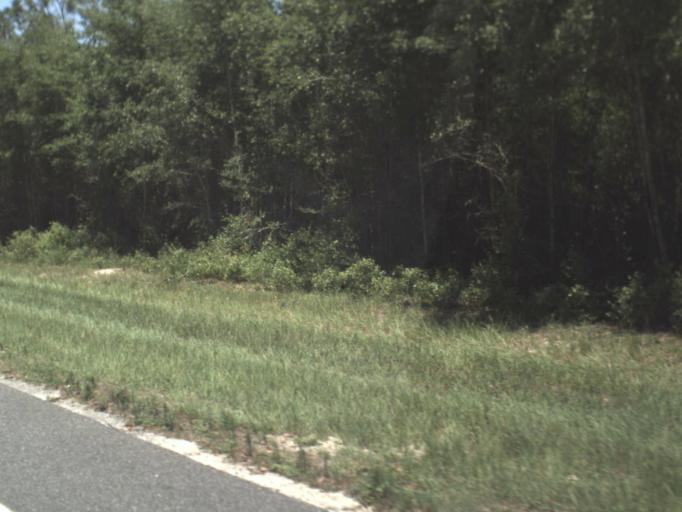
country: US
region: Florida
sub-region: Dixie County
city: Cross City
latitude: 29.8467
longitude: -82.9657
